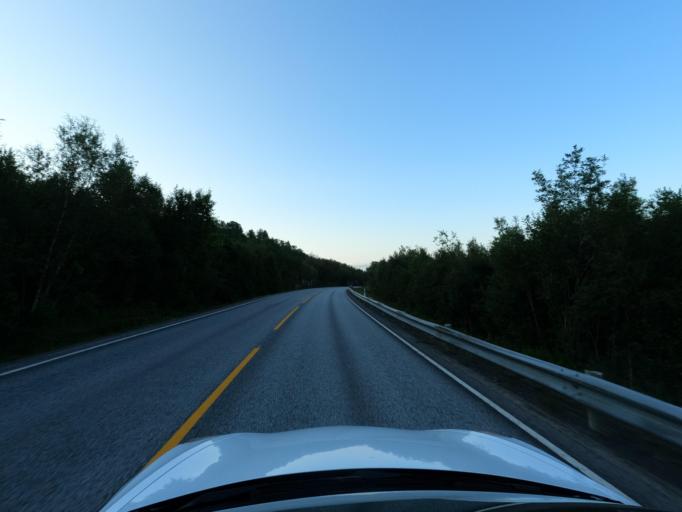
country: NO
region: Troms
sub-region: Harstad
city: Harstad
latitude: 68.7369
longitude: 16.5541
